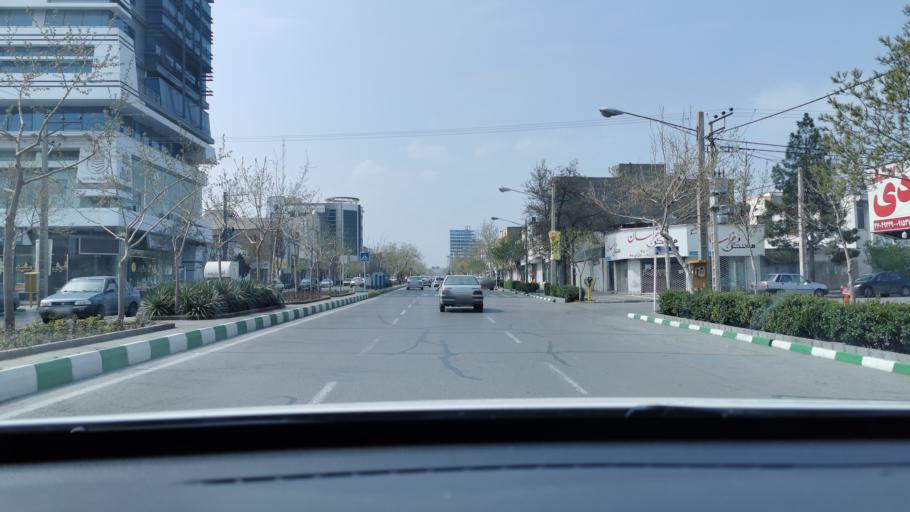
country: IR
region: Razavi Khorasan
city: Mashhad
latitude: 36.3298
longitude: 59.5240
